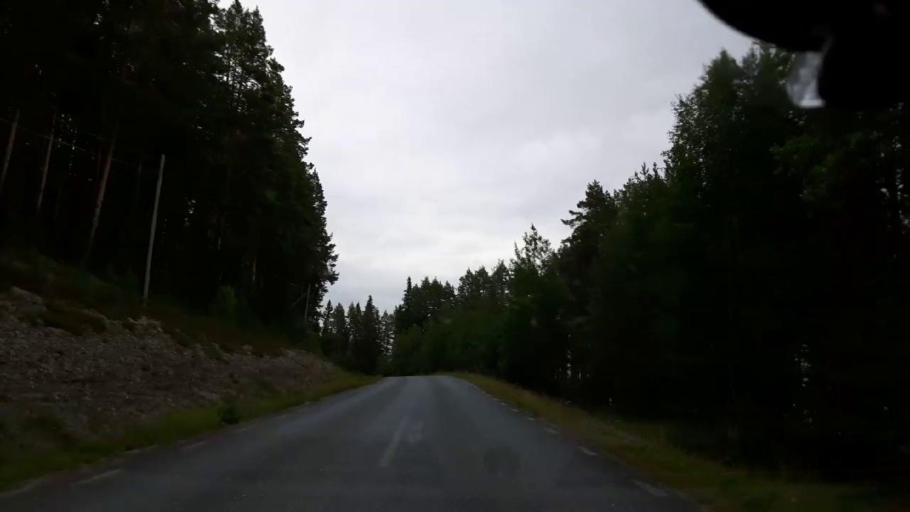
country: SE
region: Jaemtland
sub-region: Braecke Kommun
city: Braecke
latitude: 62.8610
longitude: 15.6304
